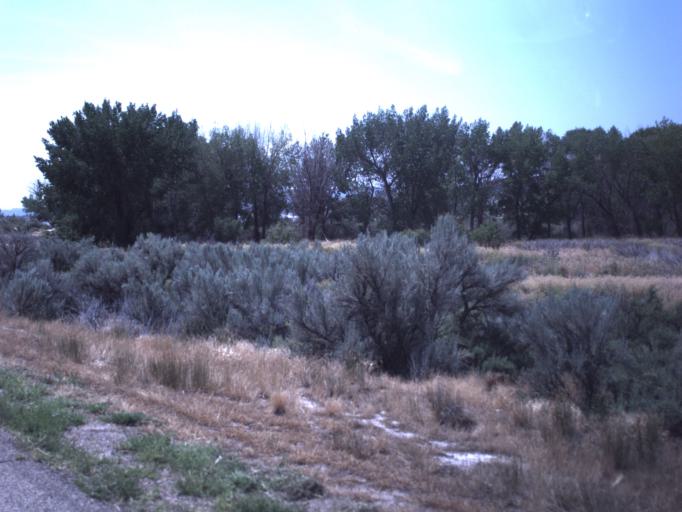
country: US
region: Utah
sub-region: Uintah County
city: Vernal
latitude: 40.5324
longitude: -109.5220
